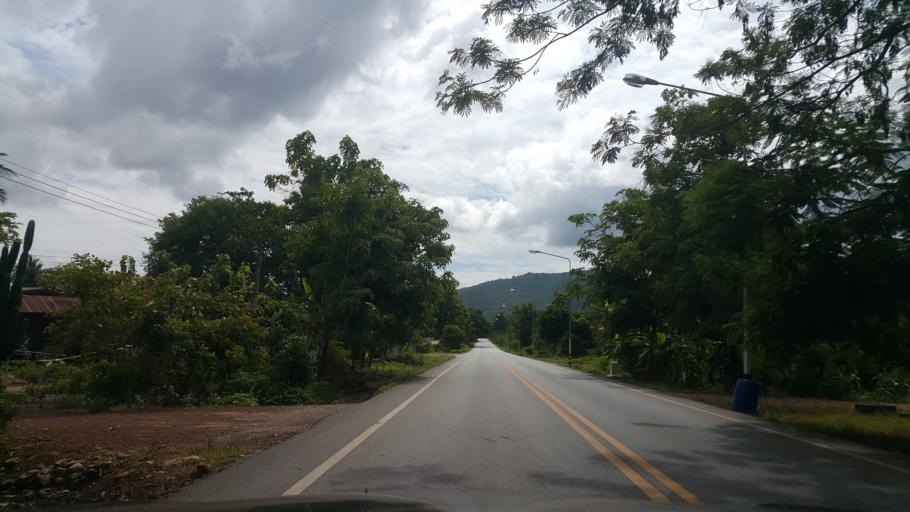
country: TH
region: Uttaradit
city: Thong Saen Khan
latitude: 17.3979
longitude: 100.3049
